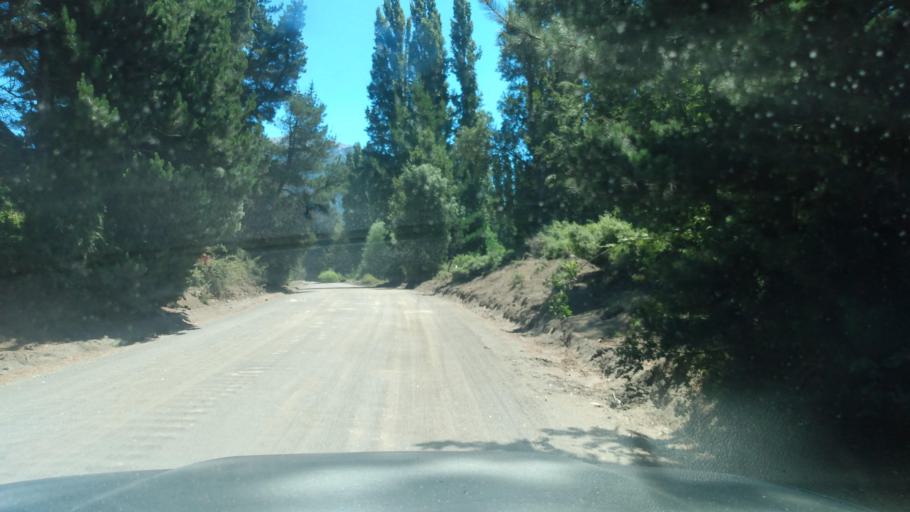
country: AR
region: Neuquen
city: Villa La Angostura
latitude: -40.6283
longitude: -71.4815
